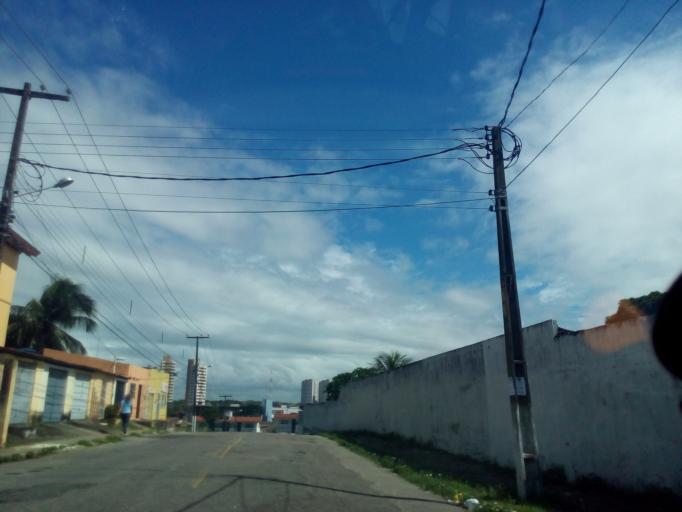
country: BR
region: Rio Grande do Norte
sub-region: Natal
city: Natal
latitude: -5.8615
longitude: -35.2041
